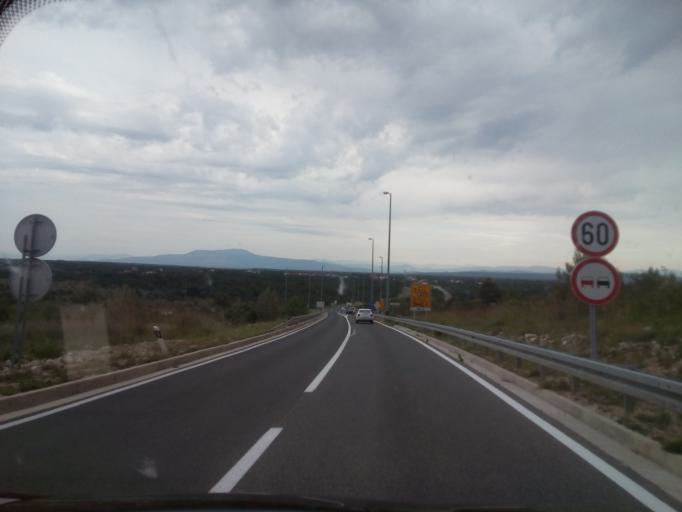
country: HR
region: Sibensko-Kniniska
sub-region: Grad Sibenik
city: Sibenik
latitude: 43.7718
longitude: 15.9471
